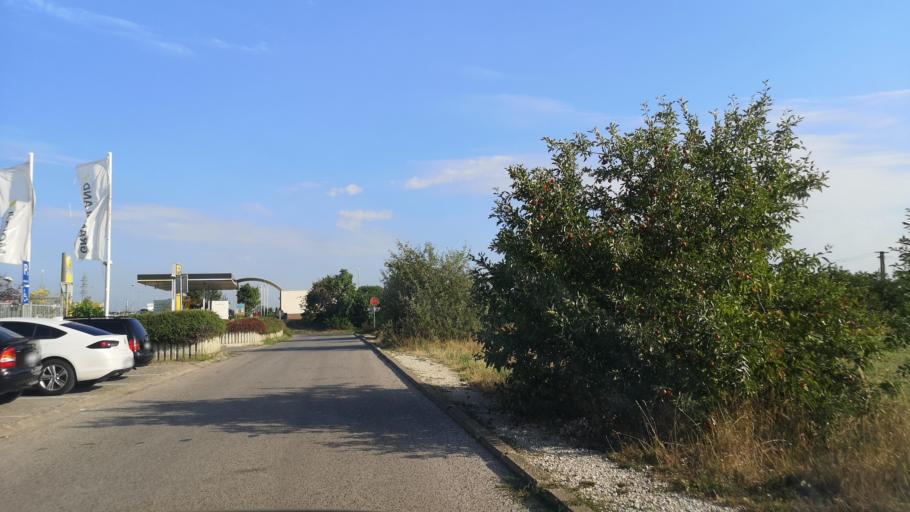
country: SK
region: Nitriansky
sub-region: Okres Nitra
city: Nitra
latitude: 48.3149
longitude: 18.0305
